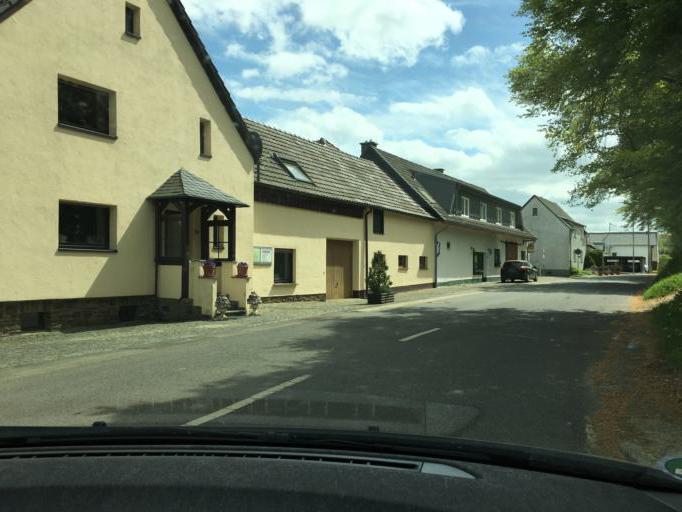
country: DE
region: Rheinland-Pfalz
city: Kirchsahr
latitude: 50.5196
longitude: 6.8613
